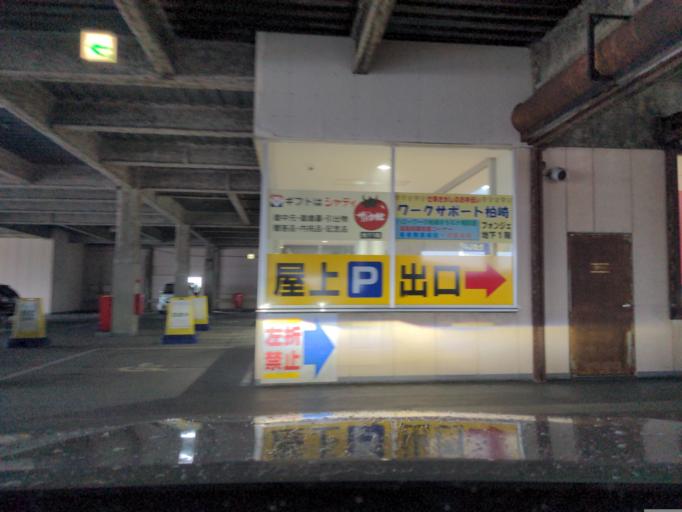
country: JP
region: Niigata
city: Kashiwazaki
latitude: 37.3694
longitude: 138.5571
